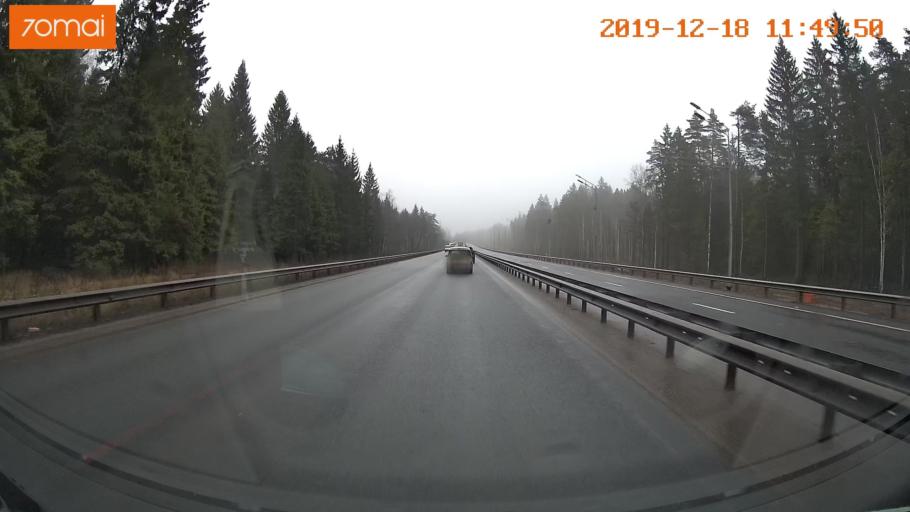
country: RU
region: Moskovskaya
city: Yershovo
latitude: 55.7808
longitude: 36.9144
